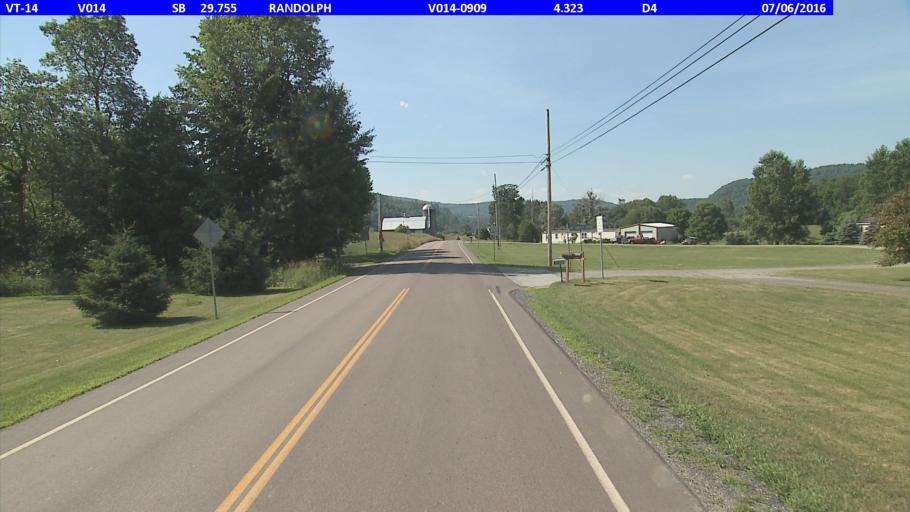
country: US
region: Vermont
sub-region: Orange County
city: Randolph
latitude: 43.9317
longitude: -72.5528
